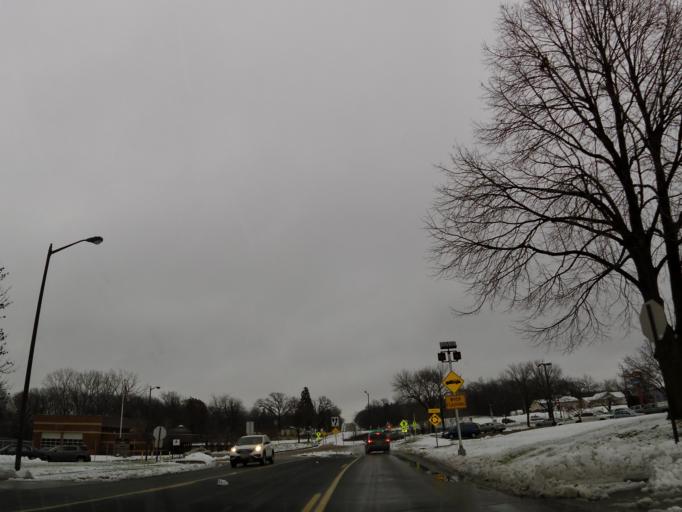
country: US
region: Minnesota
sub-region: Dakota County
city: Lakeville
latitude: 44.6958
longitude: -93.2852
